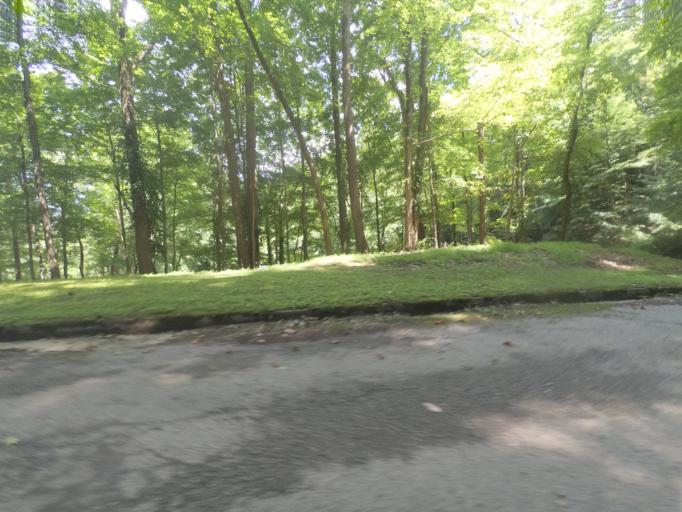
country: US
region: West Virginia
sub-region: Cabell County
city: Huntington
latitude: 38.4018
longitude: -82.4322
